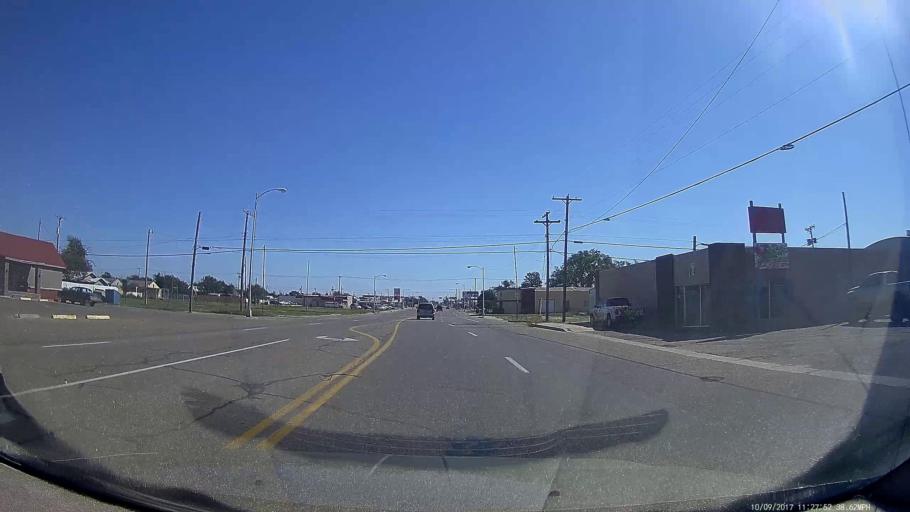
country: US
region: New Mexico
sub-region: Curry County
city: Clovis
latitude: 34.4047
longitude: -103.2221
